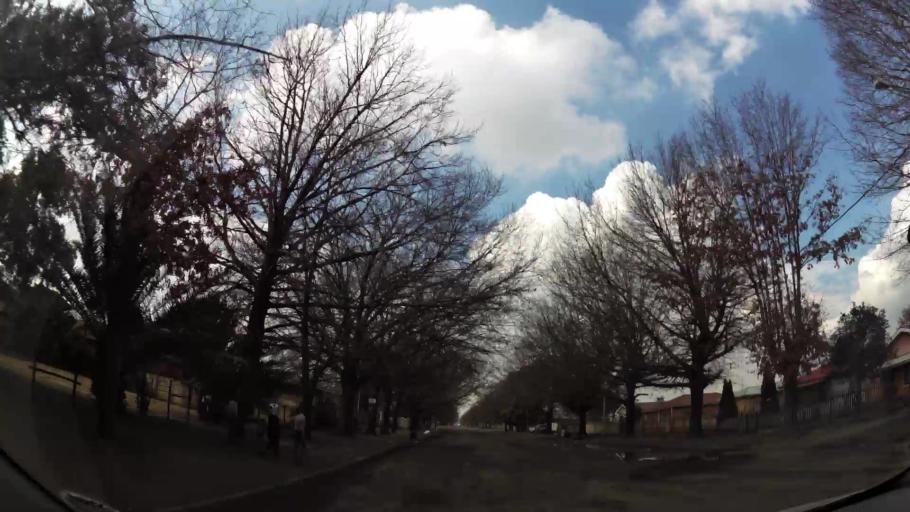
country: ZA
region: Gauteng
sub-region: Sedibeng District Municipality
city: Vereeniging
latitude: -26.6799
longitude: 27.9204
